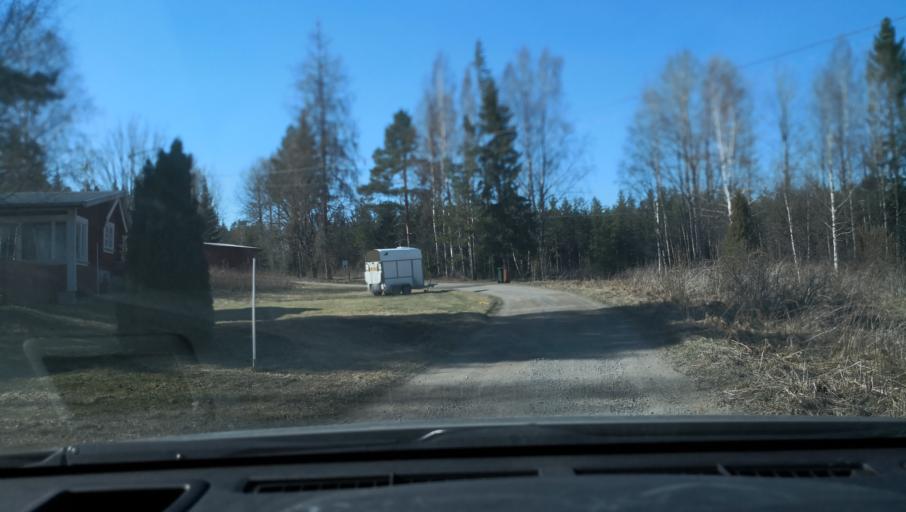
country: SE
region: Vaestmanland
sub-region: Sala Kommun
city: Sala
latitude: 59.9448
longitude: 16.4371
